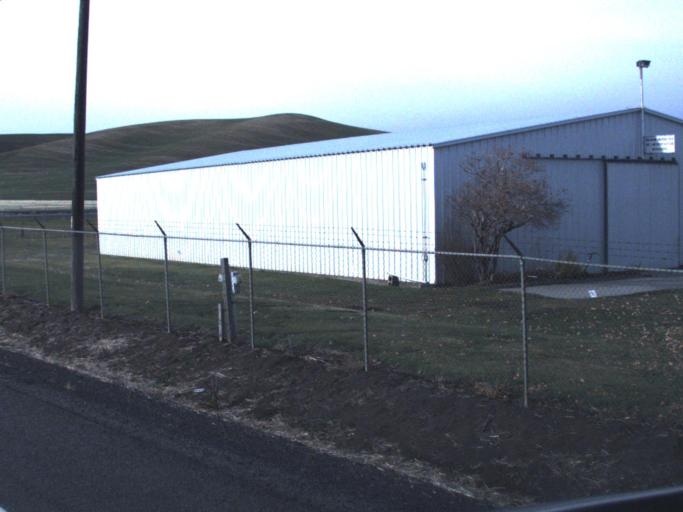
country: US
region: Washington
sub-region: Whitman County
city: Colfax
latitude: 46.8645
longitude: -117.4352
